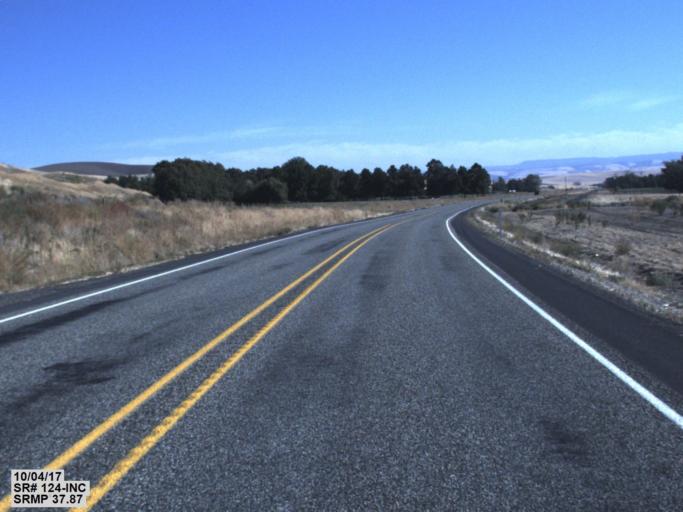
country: US
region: Washington
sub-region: Walla Walla County
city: Waitsburg
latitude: 46.2978
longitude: -118.2790
